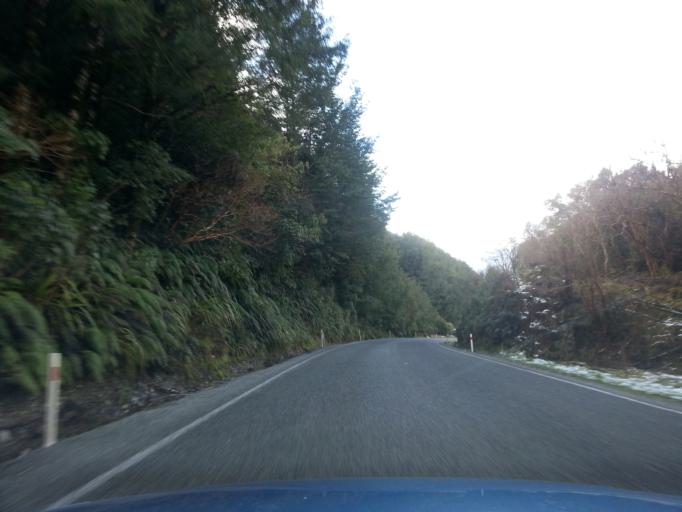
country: NZ
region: West Coast
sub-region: Grey District
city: Greymouth
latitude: -42.7794
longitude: 171.6135
